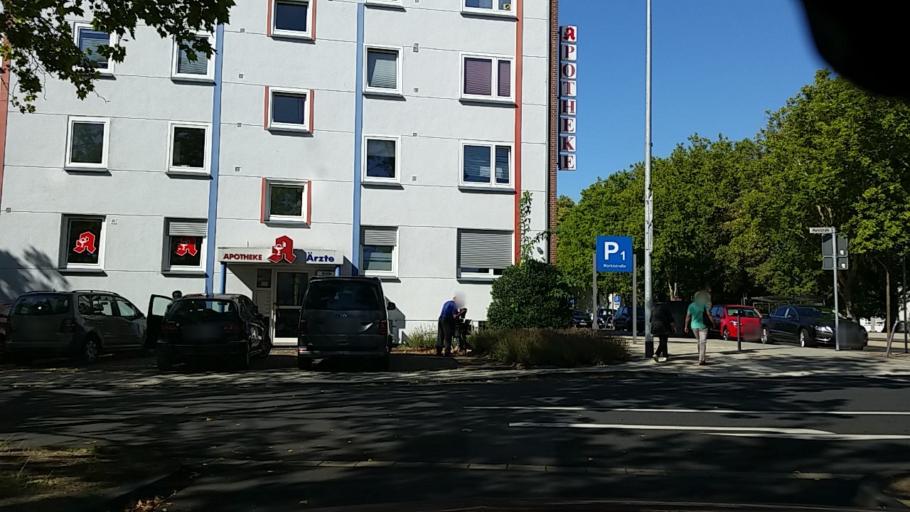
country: DE
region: Hesse
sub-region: Regierungsbezirk Kassel
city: Baunatal
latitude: 51.2556
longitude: 9.4159
